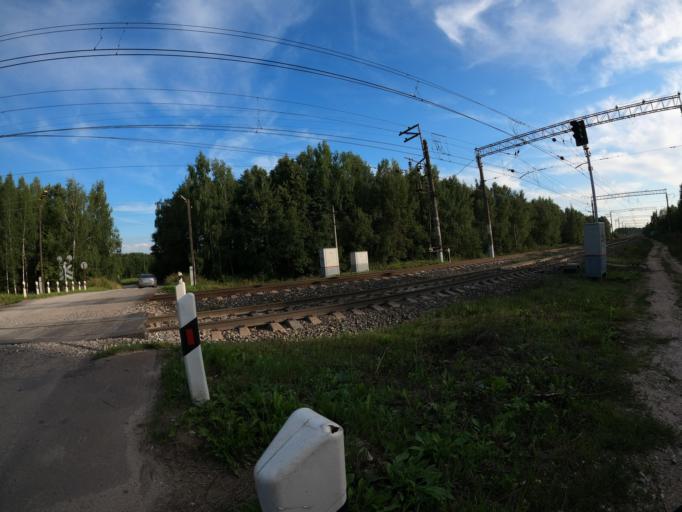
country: RU
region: Moskovskaya
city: Meshcherino
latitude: 55.1356
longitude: 38.3891
